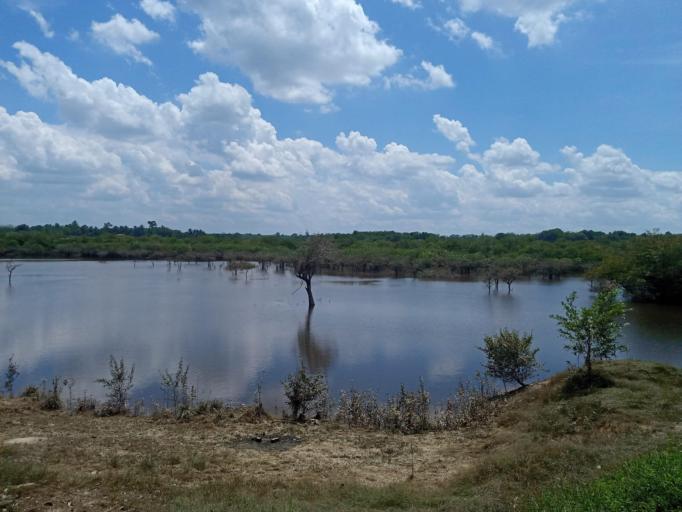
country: ID
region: Jambi
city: Sengeti
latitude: -1.4777
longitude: 103.4077
